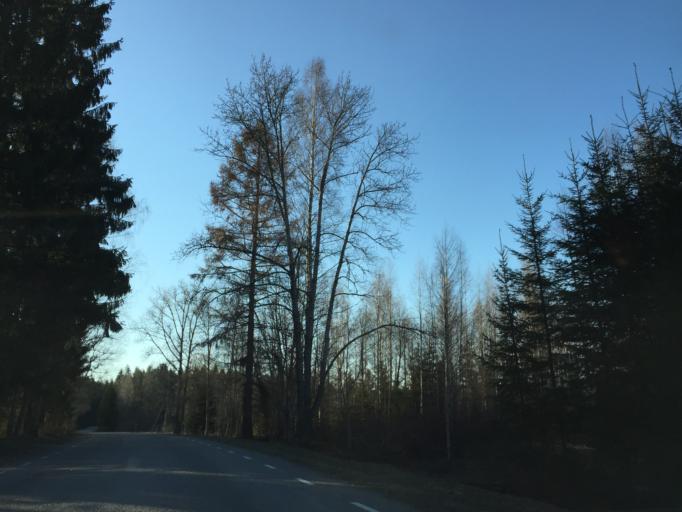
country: EE
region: Ida-Virumaa
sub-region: Toila vald
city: Voka
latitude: 59.1645
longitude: 27.5853
